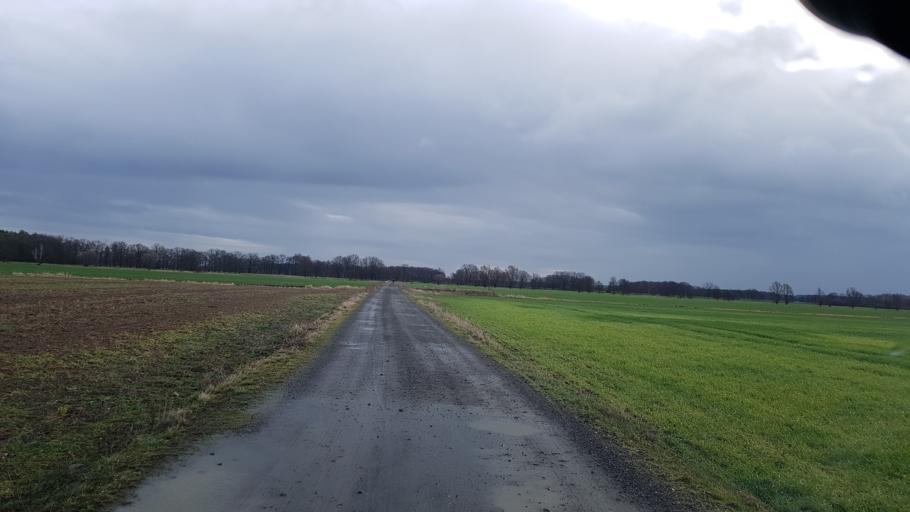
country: DE
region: Brandenburg
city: Herzberg
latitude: 51.6744
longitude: 13.2398
